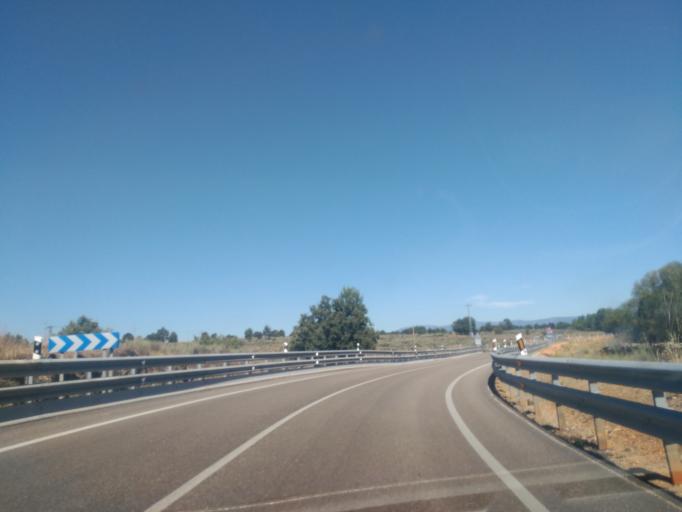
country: ES
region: Castille and Leon
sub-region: Provincia de Zamora
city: Ferreras de Arriba
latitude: 41.9567
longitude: -6.2145
